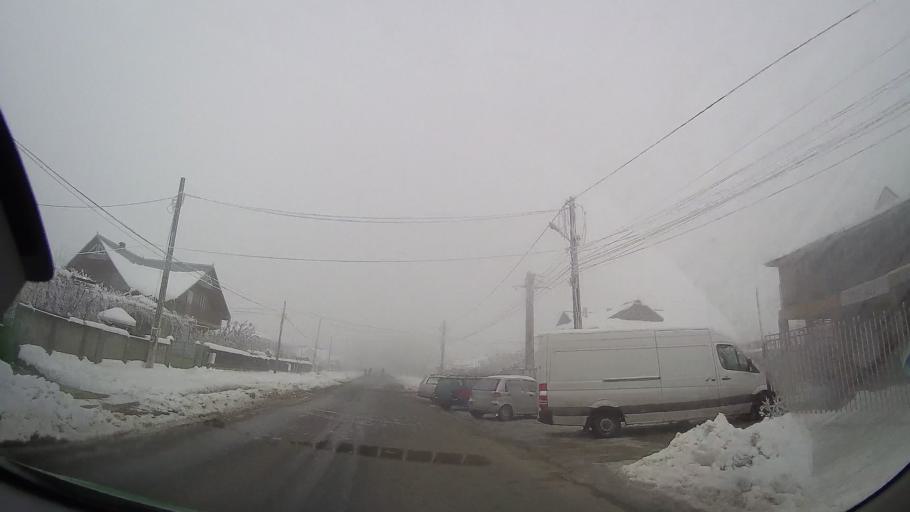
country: RO
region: Neamt
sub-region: Comuna Sabaoani
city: Sabaoani
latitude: 47.0184
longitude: 26.8655
